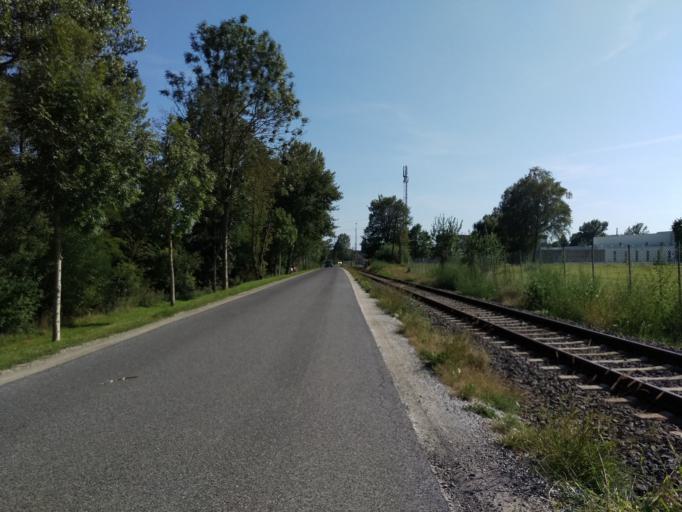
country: AT
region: Styria
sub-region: Graz Stadt
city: Graz
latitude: 47.0428
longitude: 15.4420
